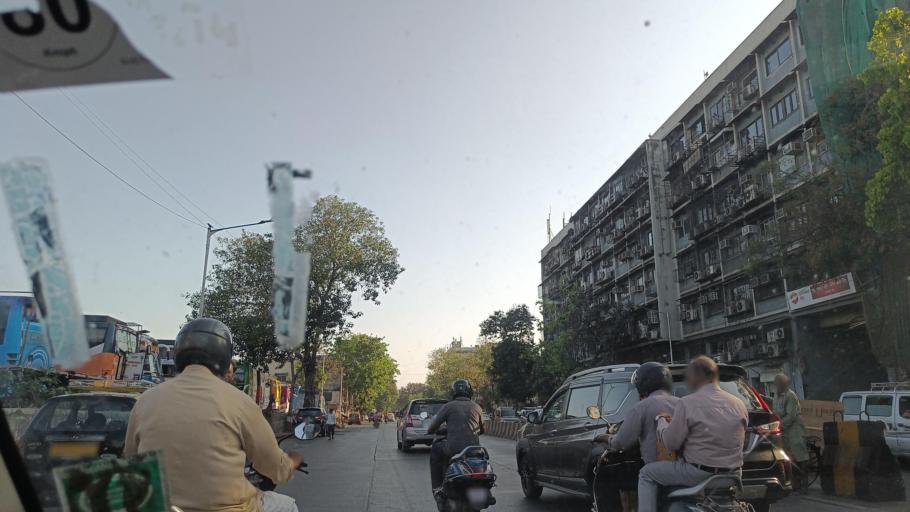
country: IN
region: Maharashtra
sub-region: Raigarh
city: Uran
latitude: 18.9514
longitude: 72.8413
